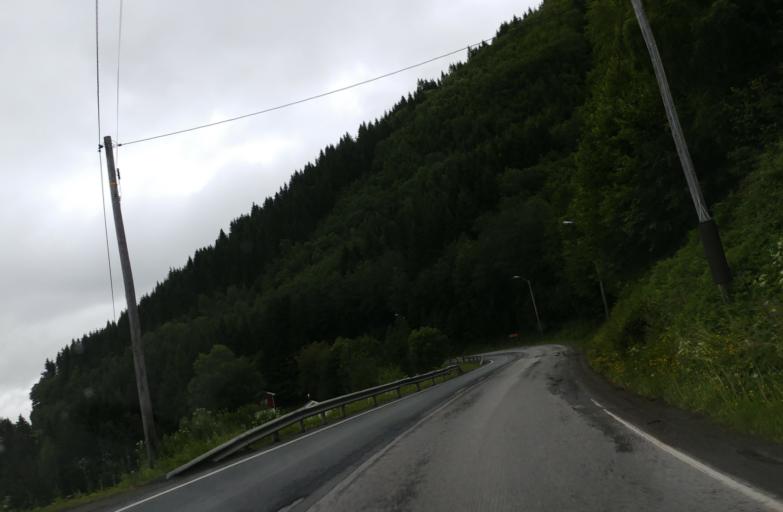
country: NO
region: Sor-Trondelag
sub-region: Selbu
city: Mebonden
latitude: 63.2388
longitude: 11.0453
